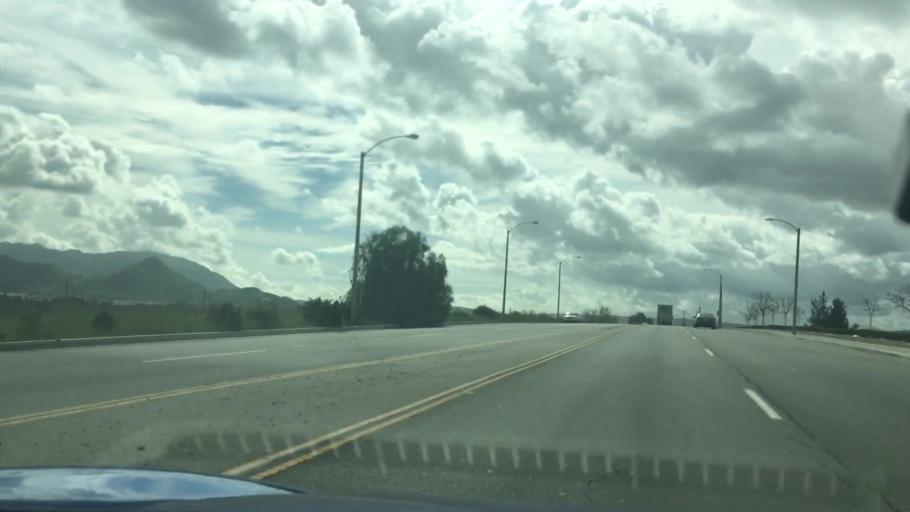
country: US
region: California
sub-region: Riverside County
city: Highgrove
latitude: 34.0288
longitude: -117.3644
